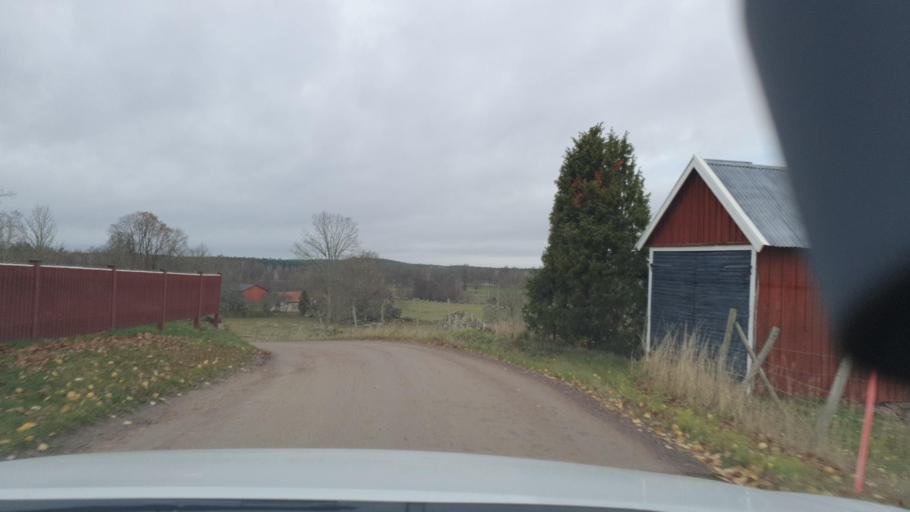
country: SE
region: Kalmar
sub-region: Hultsfreds Kommun
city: Malilla
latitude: 57.3141
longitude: 15.8161
